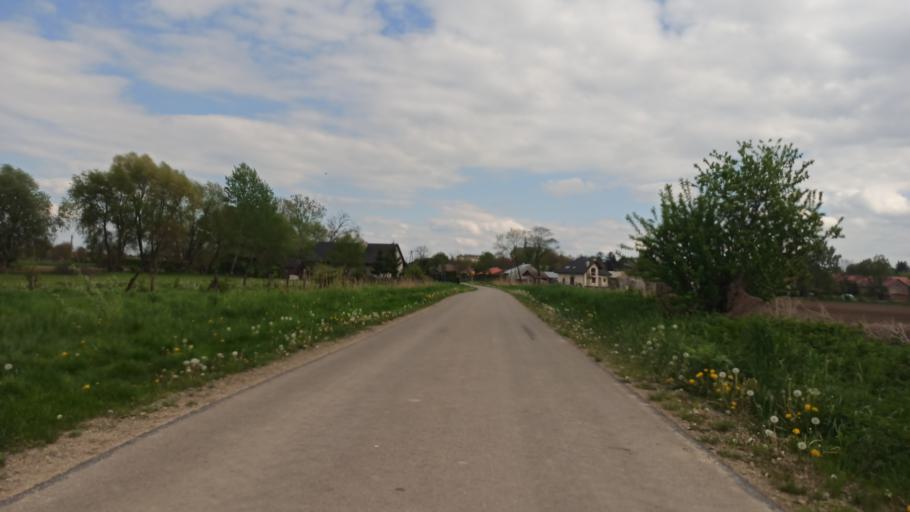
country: PL
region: Subcarpathian Voivodeship
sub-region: Powiat jaroslawski
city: Radymno
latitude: 49.9585
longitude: 22.8120
